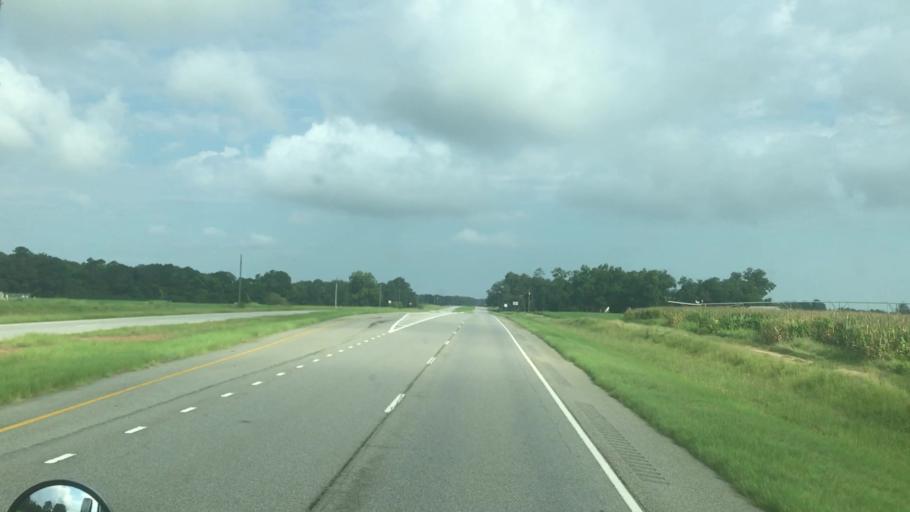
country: US
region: Georgia
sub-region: Miller County
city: Colquitt
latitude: 31.2637
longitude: -84.8164
